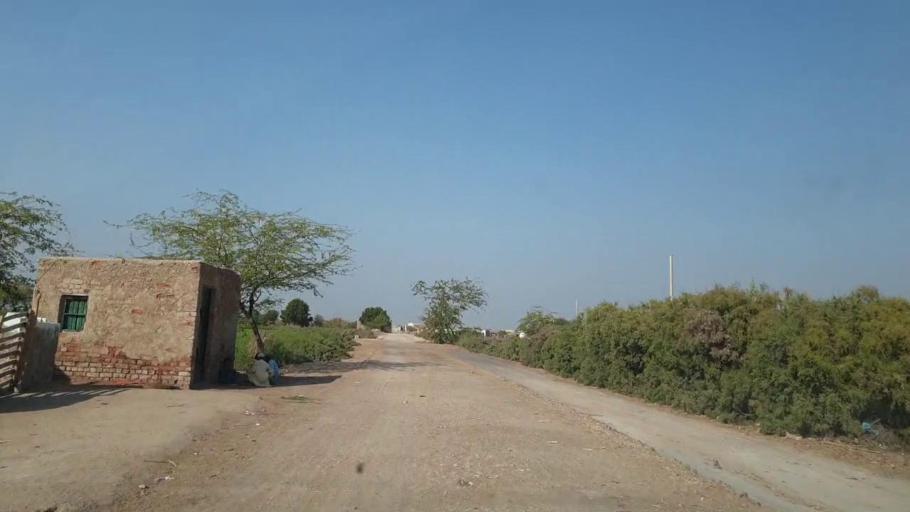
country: PK
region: Sindh
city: Tando Mittha Khan
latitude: 25.7492
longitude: 69.1966
